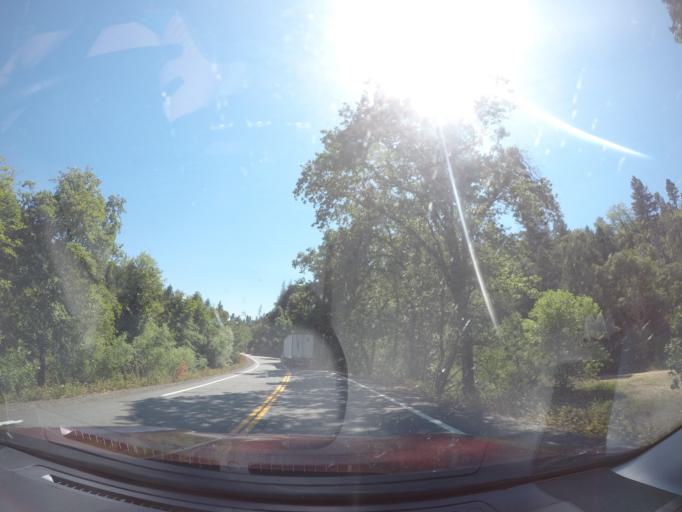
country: US
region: California
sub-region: Shasta County
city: Bella Vista
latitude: 40.7414
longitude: -122.0710
